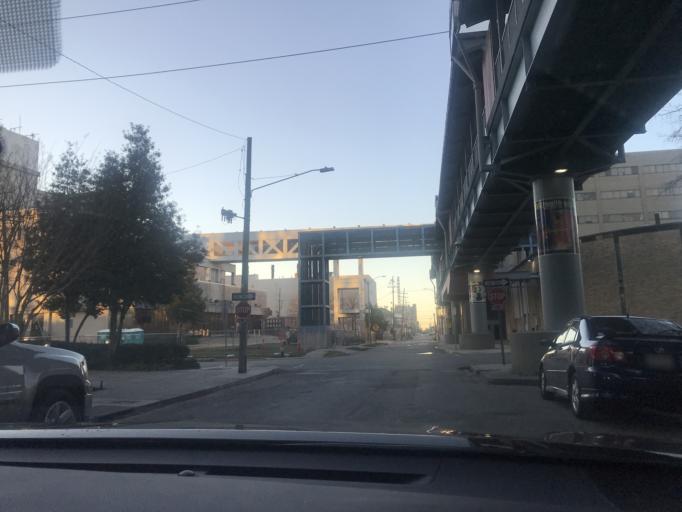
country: US
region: Louisiana
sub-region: Orleans Parish
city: New Orleans
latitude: 29.9570
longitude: -90.0837
